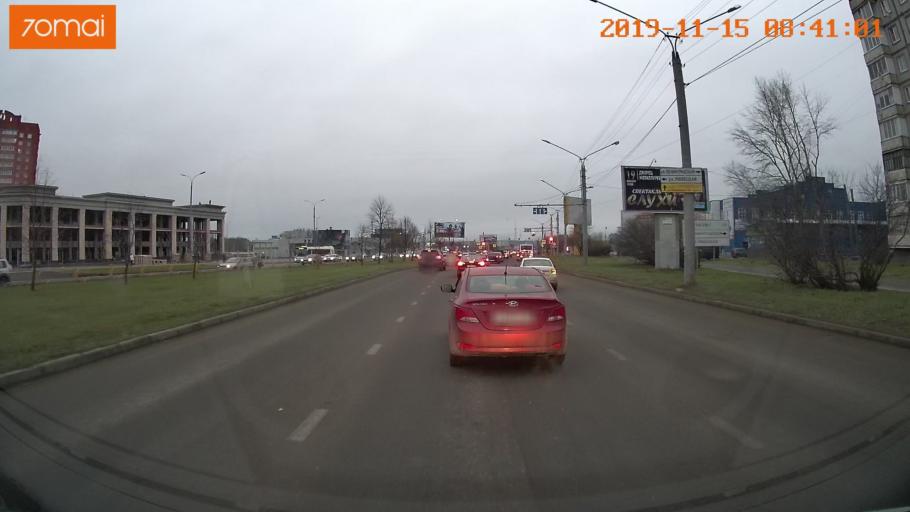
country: RU
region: Vologda
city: Cherepovets
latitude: 59.0971
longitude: 37.9122
